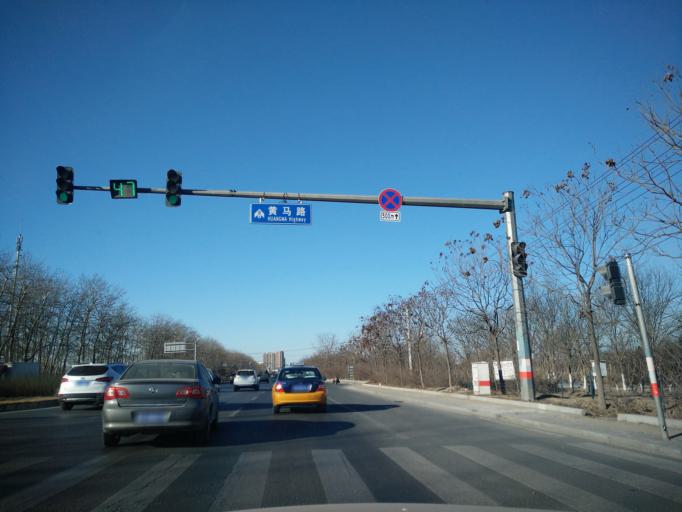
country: CN
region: Beijing
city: Xingfeng
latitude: 39.7208
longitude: 116.3601
